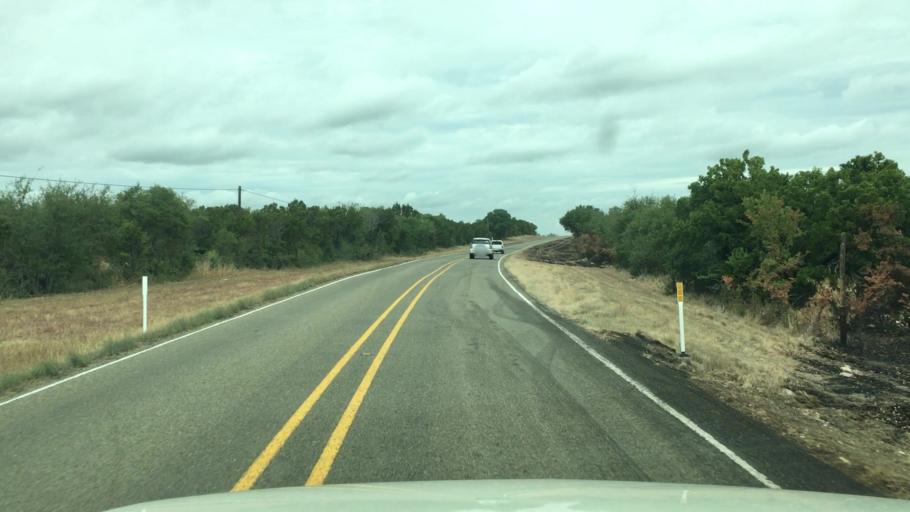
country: US
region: Texas
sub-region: Llano County
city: Horseshoe Bay
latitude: 30.4842
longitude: -98.4290
